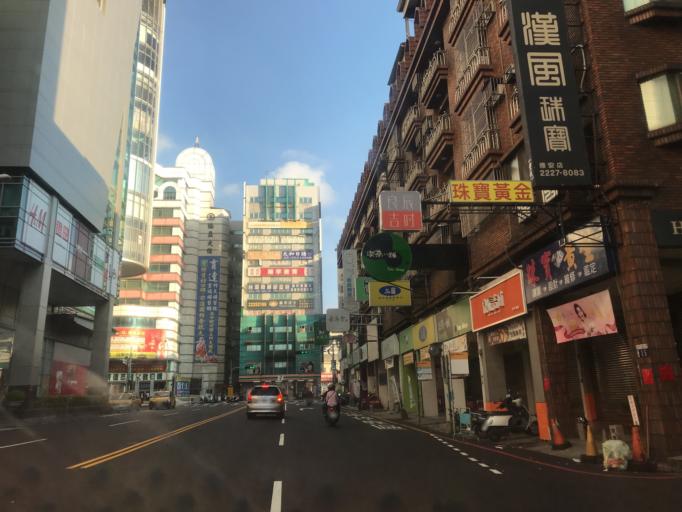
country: TW
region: Taiwan
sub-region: Taichung City
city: Taichung
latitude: 24.1357
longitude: 120.6882
